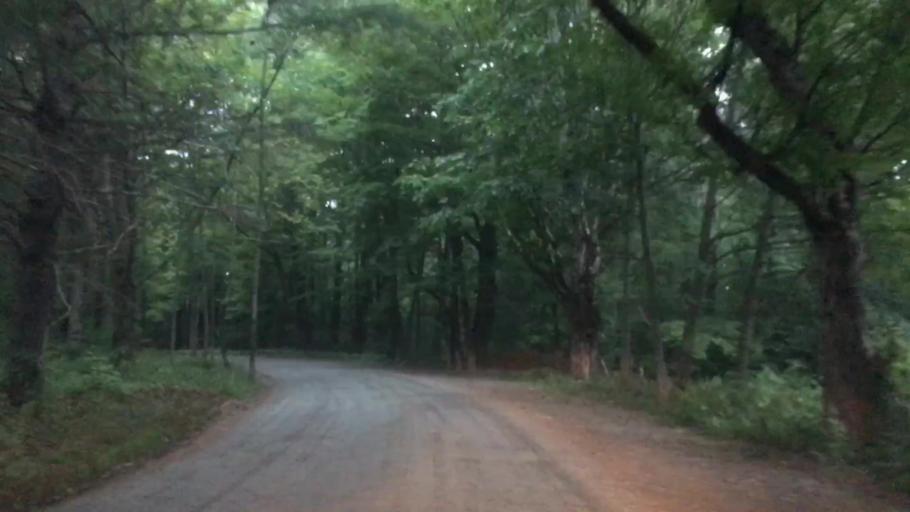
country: US
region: Vermont
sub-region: Windham County
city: Dover
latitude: 42.8229
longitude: -72.7613
